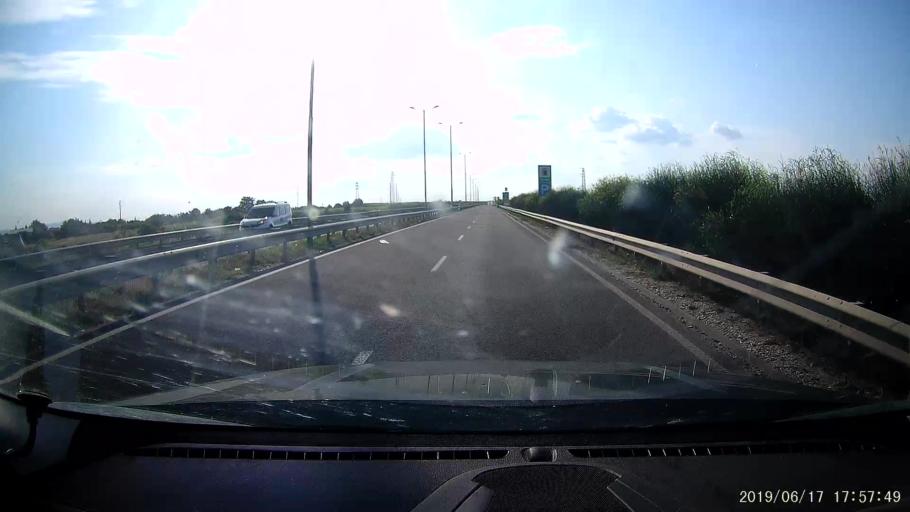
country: BG
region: Khaskovo
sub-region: Obshtina Svilengrad
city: Svilengrad
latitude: 41.7232
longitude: 26.3299
